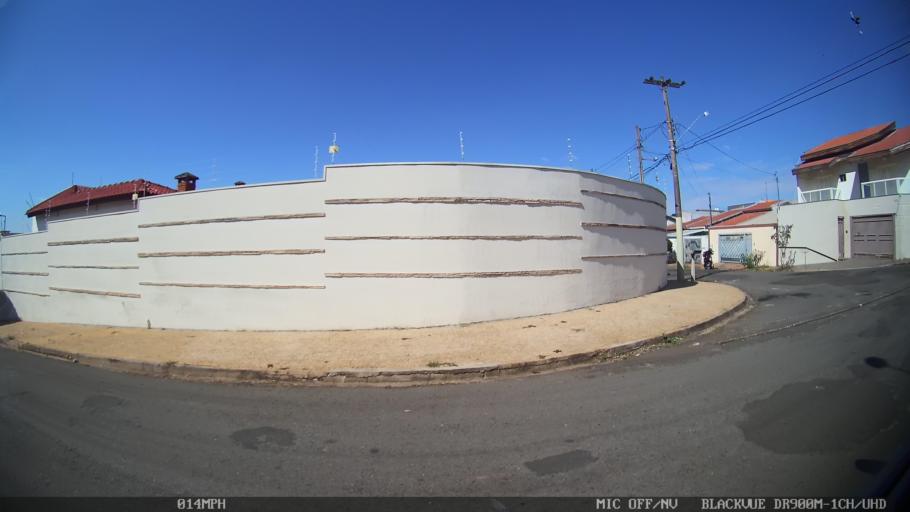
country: BR
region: Sao Paulo
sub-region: Santa Barbara D'Oeste
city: Santa Barbara d'Oeste
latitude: -22.7400
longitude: -47.4223
